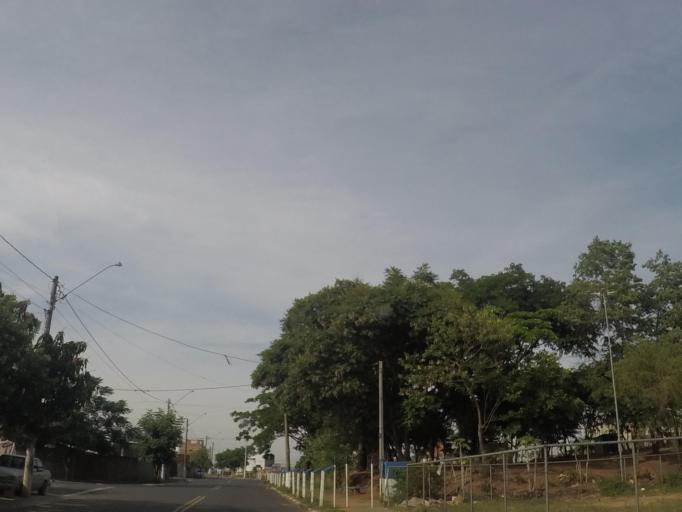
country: BR
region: Sao Paulo
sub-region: Hortolandia
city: Hortolandia
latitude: -22.8503
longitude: -47.1962
